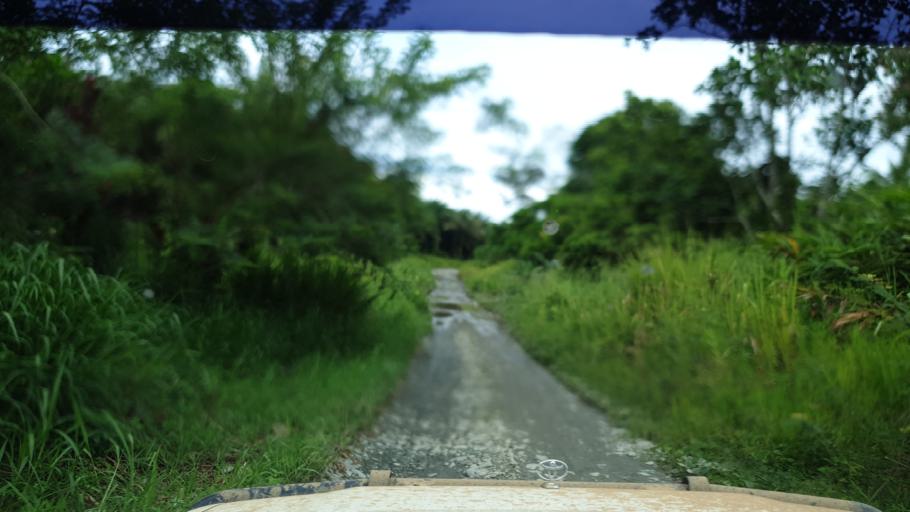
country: PG
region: Northern Province
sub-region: Sohe
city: Kokoda
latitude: -8.9172
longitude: 147.8614
